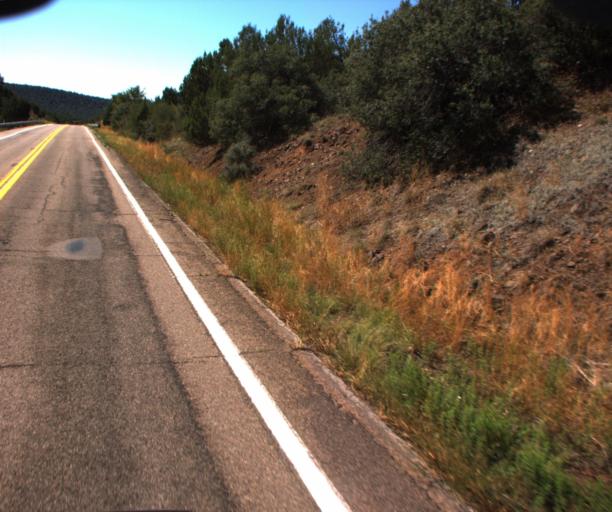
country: US
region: Arizona
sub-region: Navajo County
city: Cibecue
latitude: 33.9159
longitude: -110.3639
